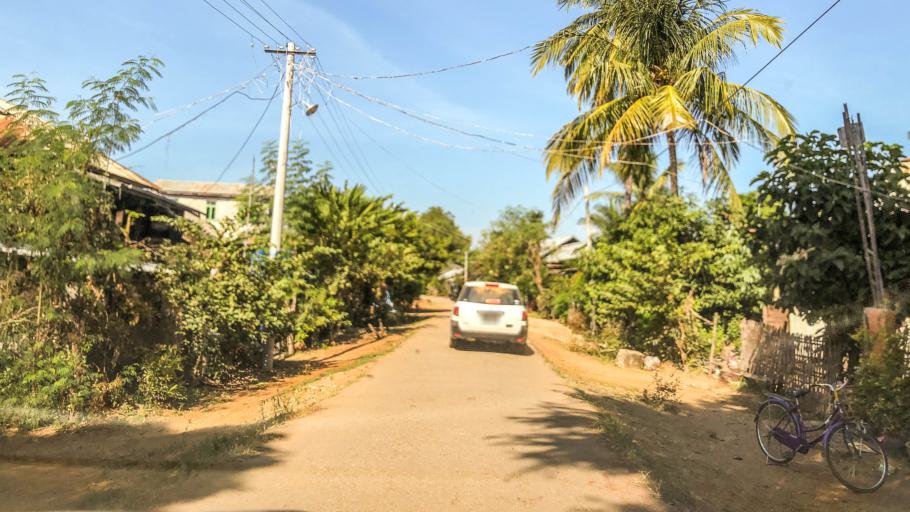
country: MM
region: Magway
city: Magway
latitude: 19.9723
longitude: 95.0410
